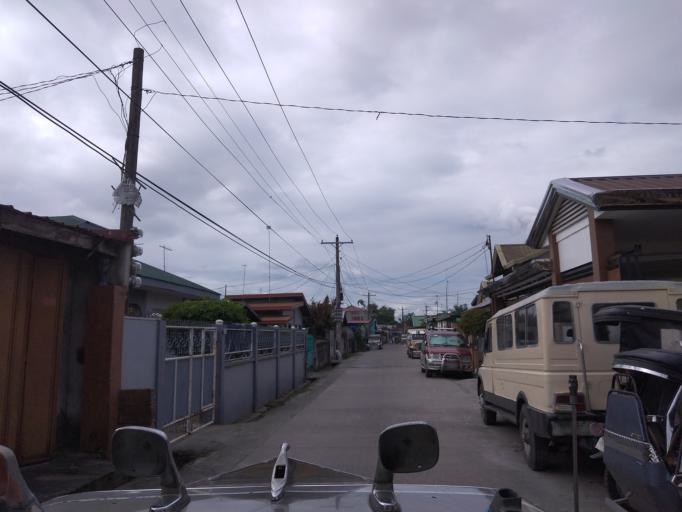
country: PH
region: Central Luzon
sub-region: Province of Pampanga
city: Pandacaqui
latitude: 15.1826
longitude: 120.6450
